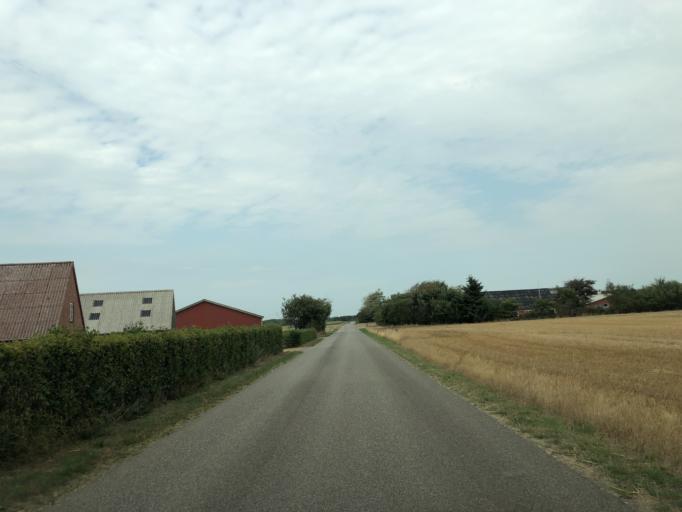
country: DK
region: Central Jutland
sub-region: Holstebro Kommune
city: Ulfborg
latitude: 56.1690
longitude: 8.3256
